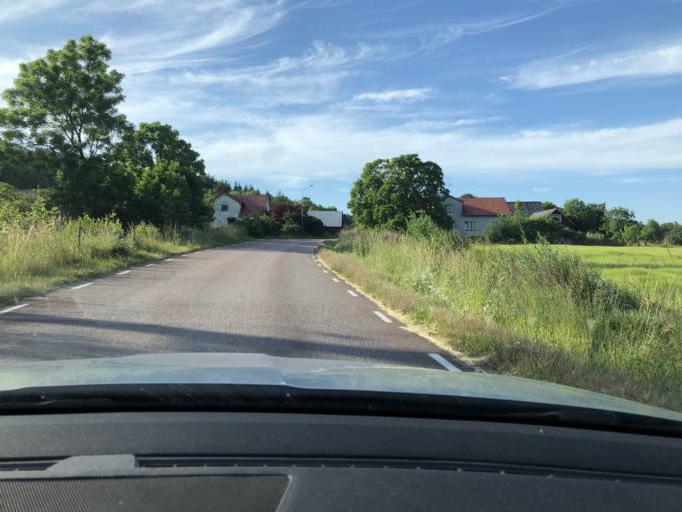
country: SE
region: Blekinge
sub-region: Solvesborgs Kommun
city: Soelvesborg
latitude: 56.1333
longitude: 14.6070
